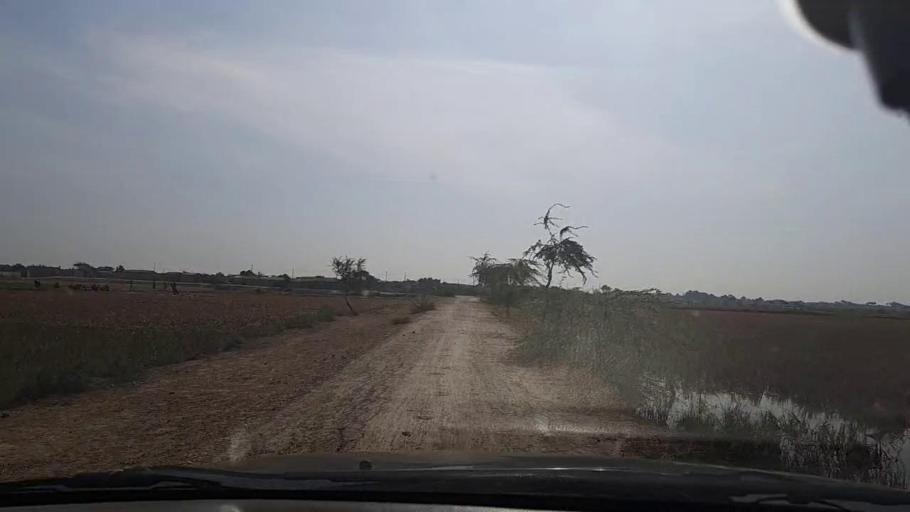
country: PK
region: Sindh
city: Mirpur Batoro
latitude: 24.7464
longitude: 68.2704
